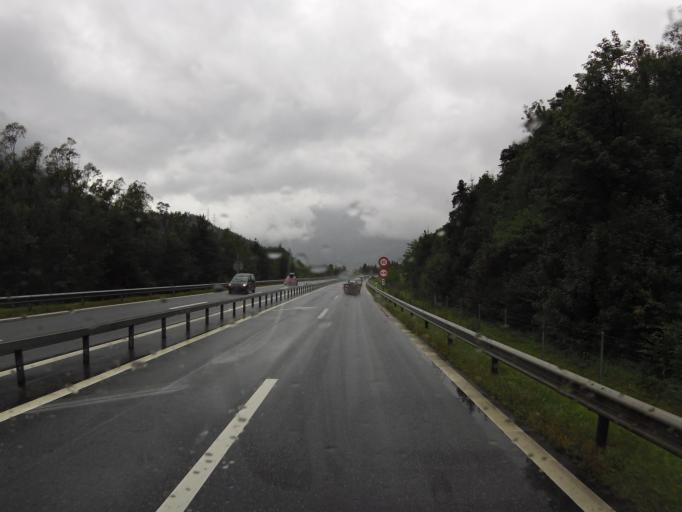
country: CH
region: Grisons
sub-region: Imboden District
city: Rhazuns
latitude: 46.7780
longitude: 9.4174
